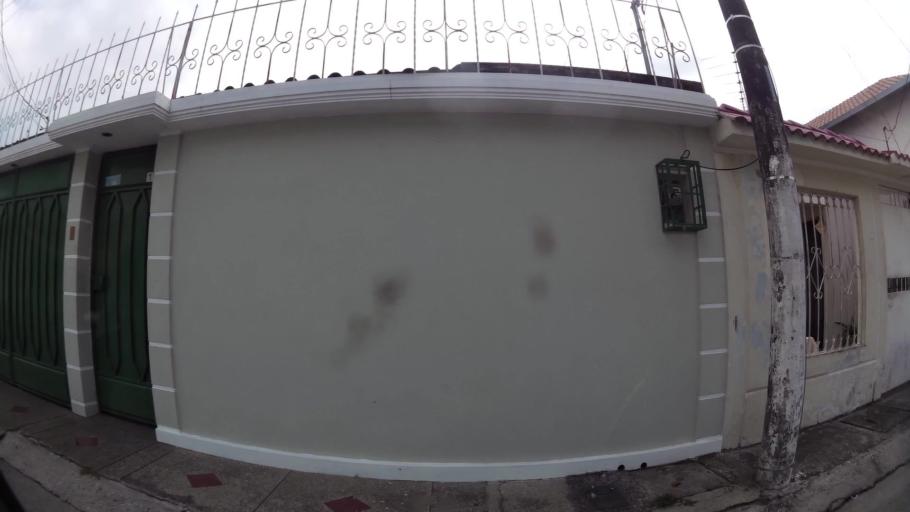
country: EC
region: Guayas
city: Eloy Alfaro
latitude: -2.1169
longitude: -79.8921
